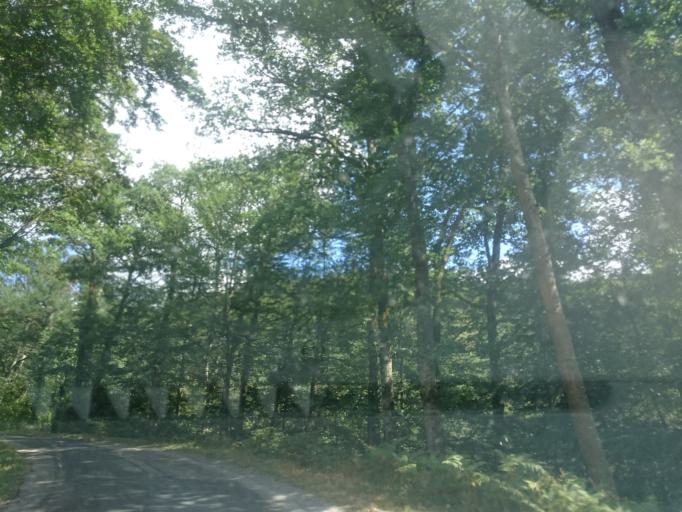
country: FR
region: Auvergne
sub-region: Departement du Cantal
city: Saint-Mamet-la-Salvetat
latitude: 44.8819
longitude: 2.2475
